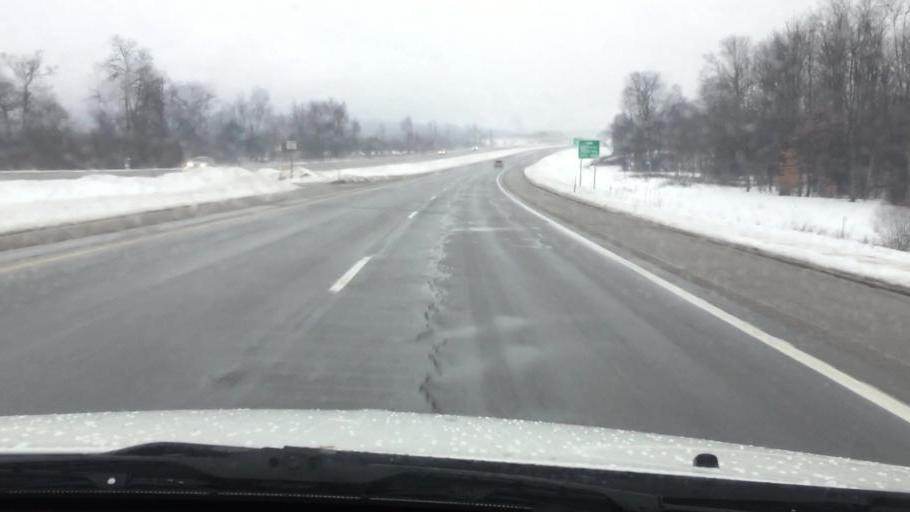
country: US
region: Michigan
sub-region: Wexford County
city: Cadillac
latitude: 44.2927
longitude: -85.3891
